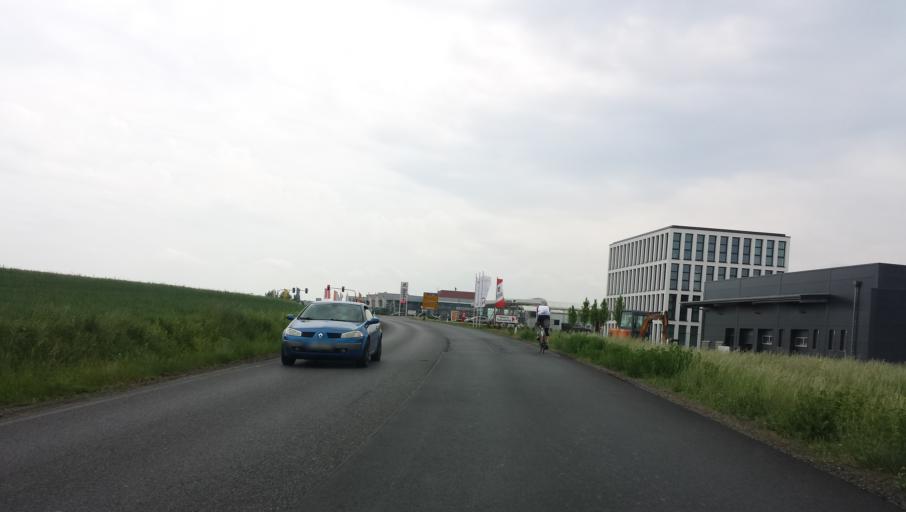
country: DE
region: Hesse
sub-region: Regierungsbezirk Darmstadt
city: Bad Vilbel
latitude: 50.1947
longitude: 8.7227
